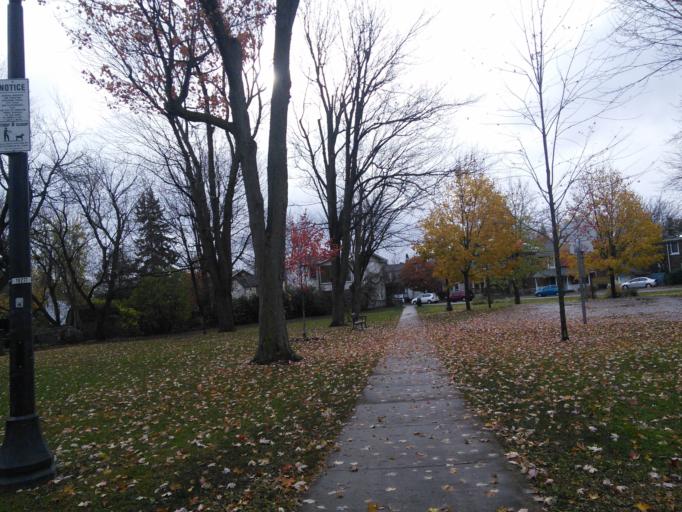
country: CA
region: Ontario
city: Kingston
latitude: 44.2357
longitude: -76.4881
